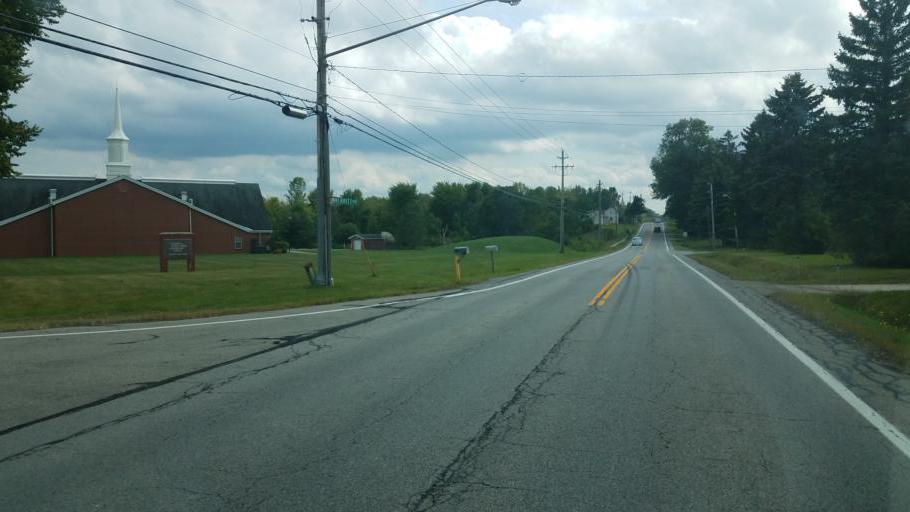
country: US
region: Ohio
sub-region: Geauga County
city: Burton
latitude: 41.5037
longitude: -81.1936
